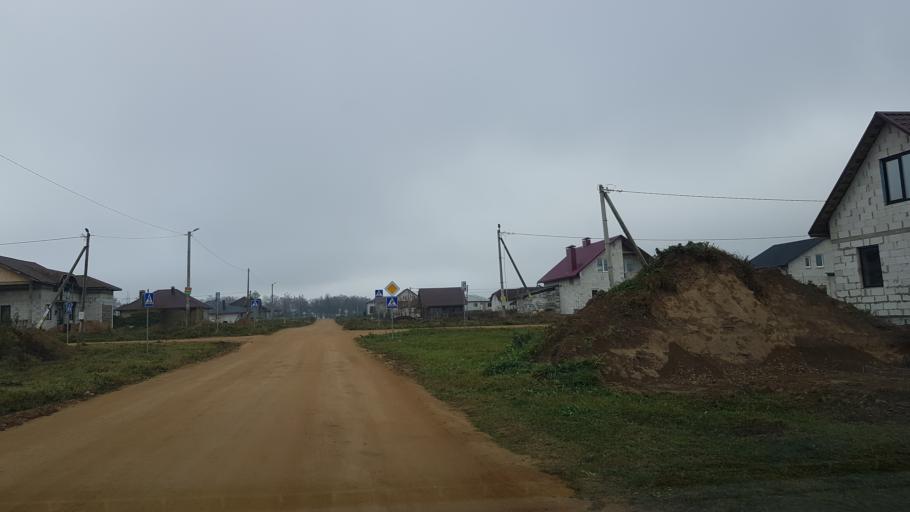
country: BY
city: Fanipol
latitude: 53.7307
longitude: 27.3249
